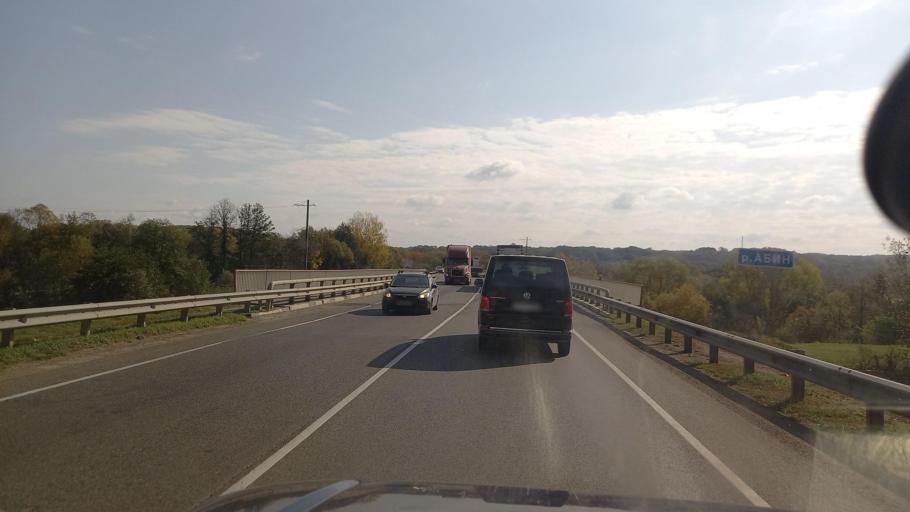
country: RU
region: Krasnodarskiy
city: Abinsk
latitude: 44.8412
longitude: 38.1612
